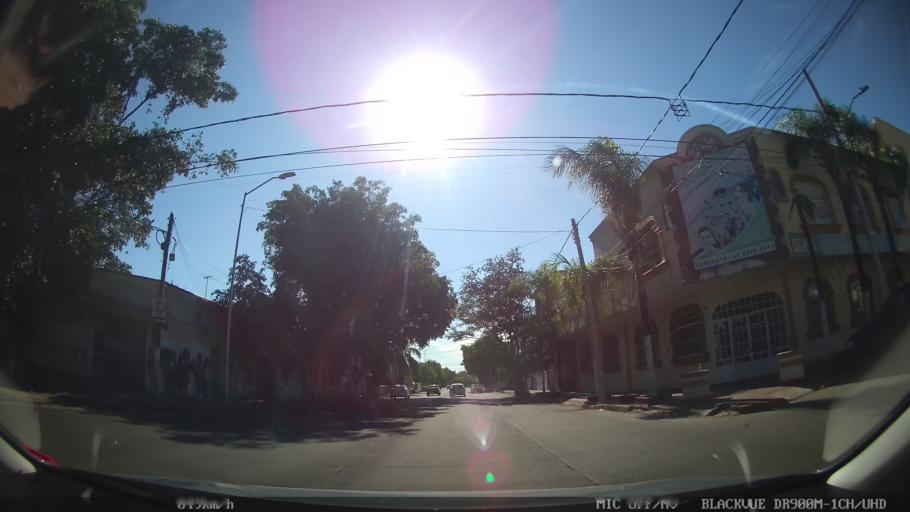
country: MX
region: Jalisco
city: Tlaquepaque
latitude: 20.6694
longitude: -103.3193
